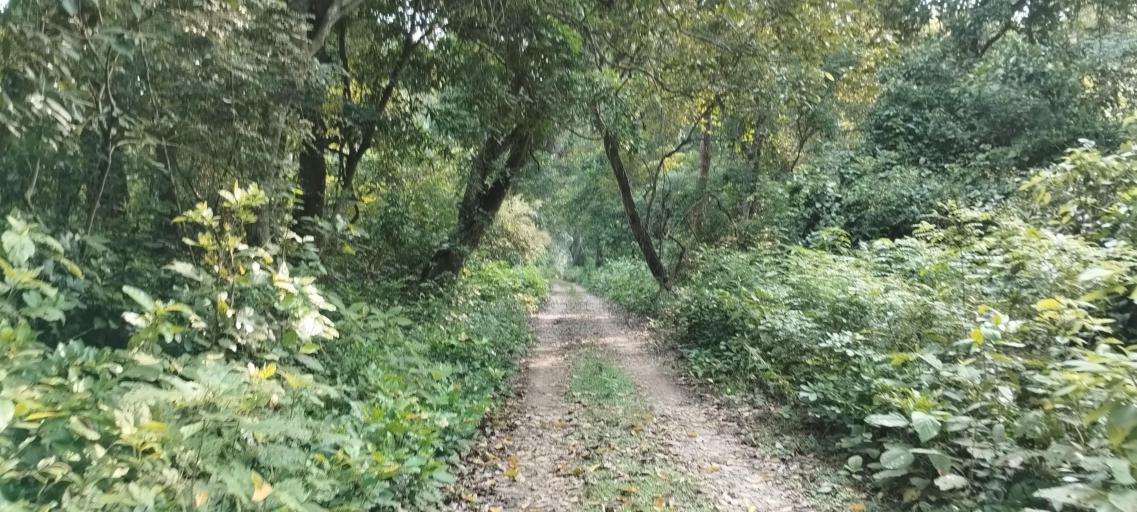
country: NP
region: Far Western
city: Tikapur
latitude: 28.4626
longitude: 81.2414
